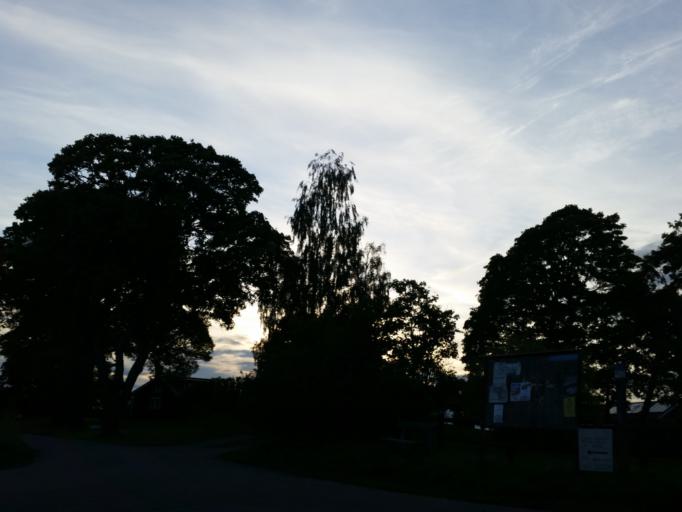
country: SE
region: Stockholm
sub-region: Sigtuna Kommun
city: Marsta
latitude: 59.6385
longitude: 17.8805
